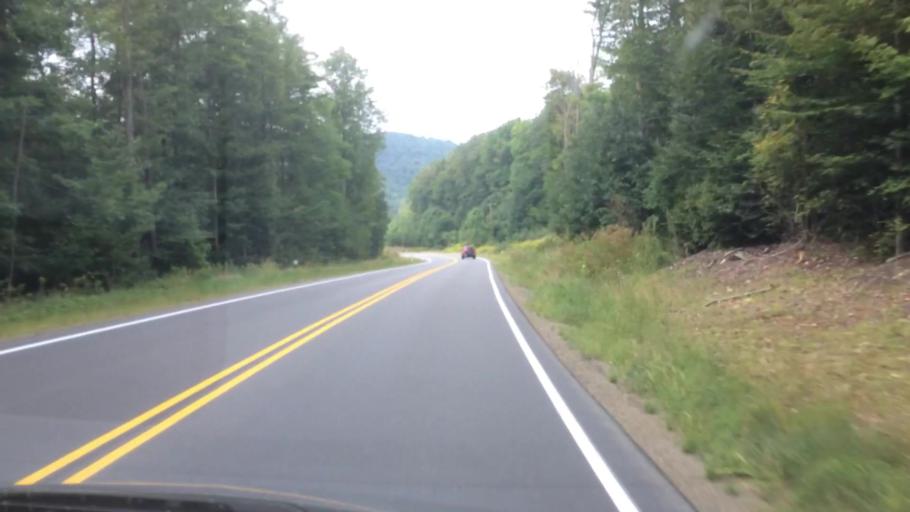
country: US
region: Pennsylvania
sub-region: McKean County
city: Bradford
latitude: 41.8866
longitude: -78.5940
